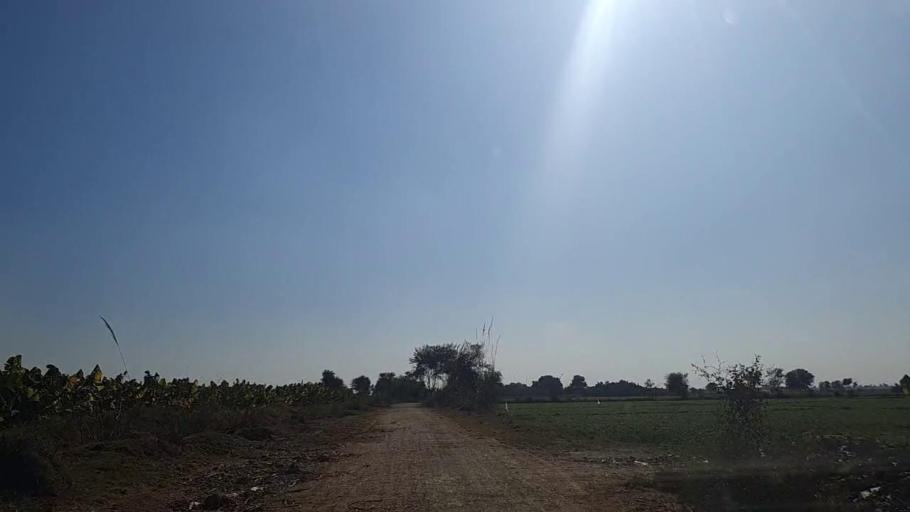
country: PK
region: Sindh
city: Sakrand
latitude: 26.2378
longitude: 68.1997
